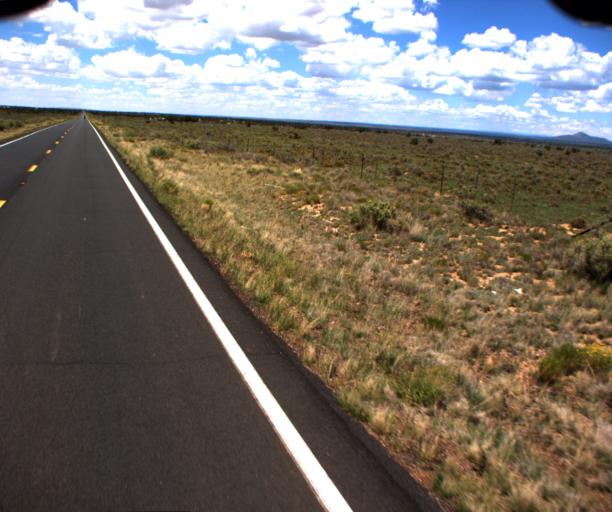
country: US
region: Arizona
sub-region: Coconino County
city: Williams
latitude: 35.6300
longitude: -112.1169
